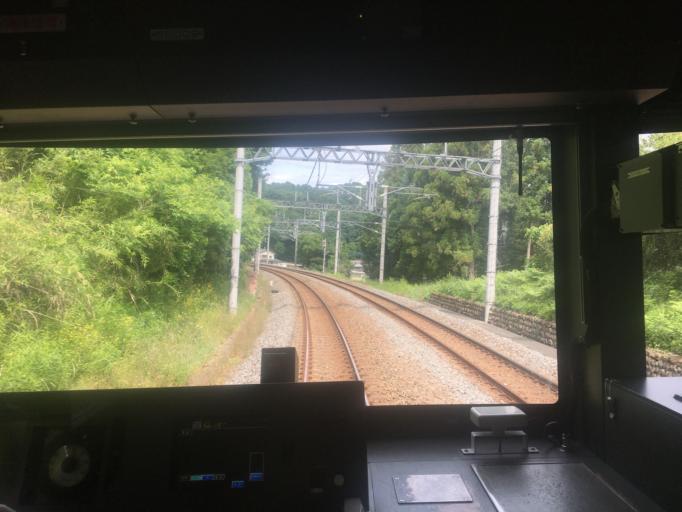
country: JP
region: Saitama
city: Ogawa
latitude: 36.0513
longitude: 139.3145
